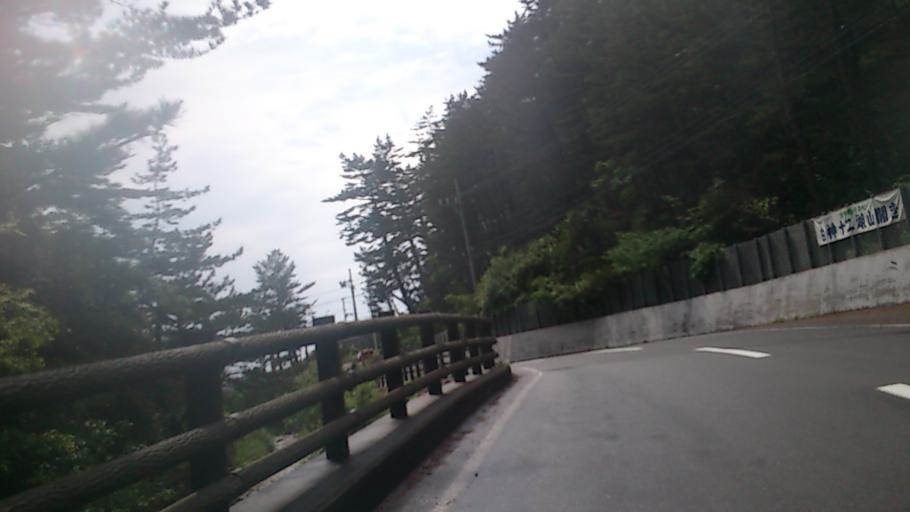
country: JP
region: Akita
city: Noshiromachi
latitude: 40.5506
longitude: 139.9450
